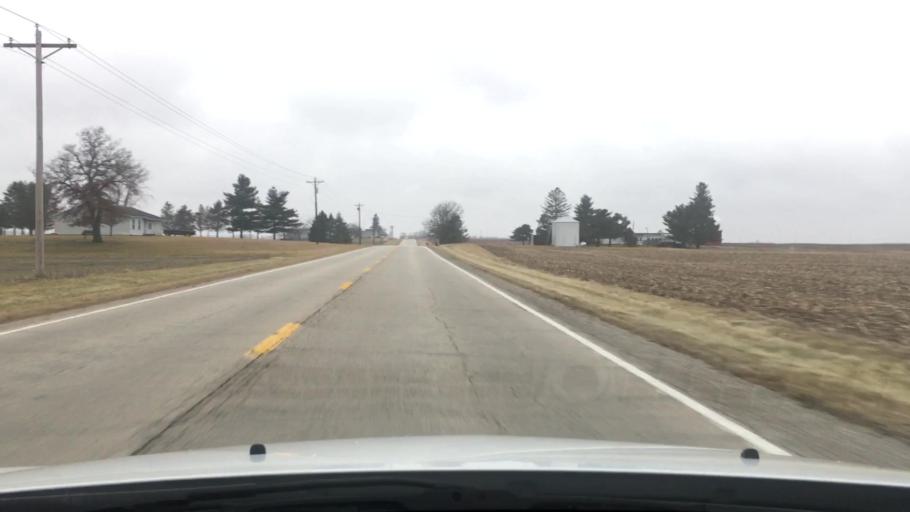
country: US
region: Illinois
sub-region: Iroquois County
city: Watseka
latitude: 40.8905
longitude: -87.7031
